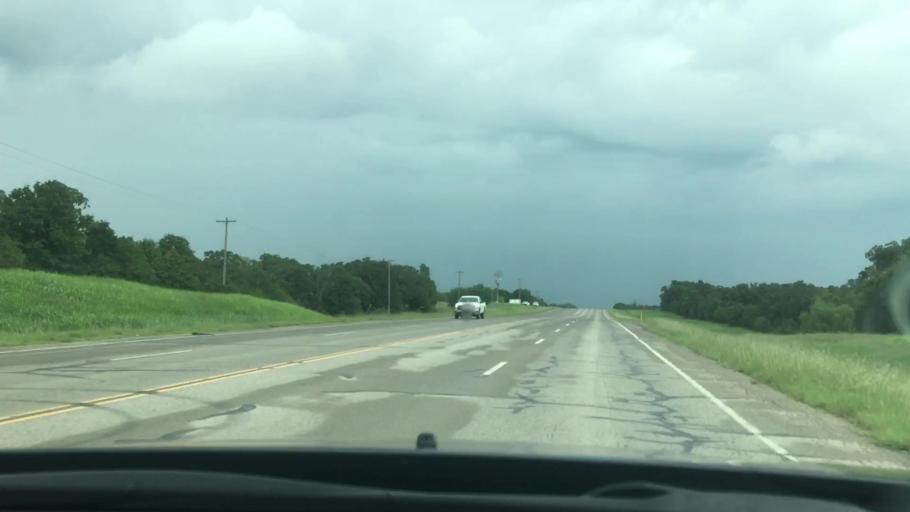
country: US
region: Oklahoma
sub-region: Carter County
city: Healdton
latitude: 34.1839
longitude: -97.4747
